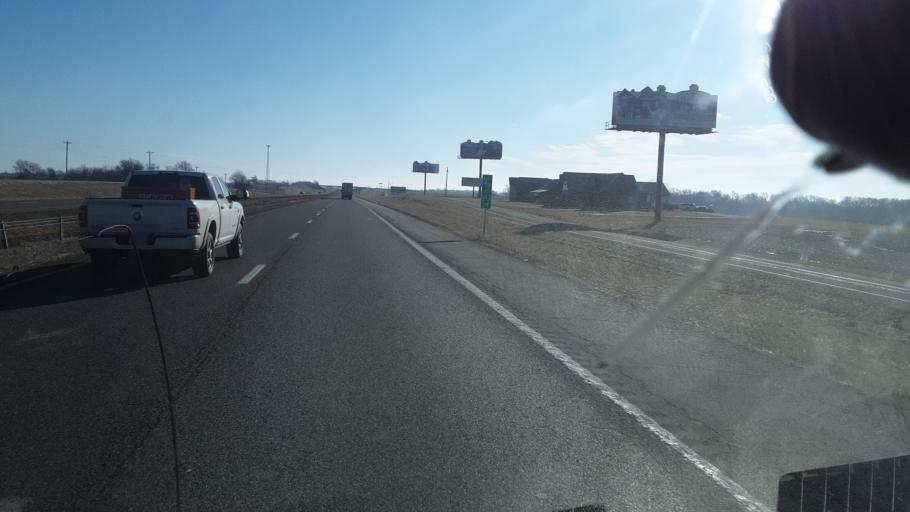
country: US
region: Missouri
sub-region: Callaway County
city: Fulton
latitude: 38.9519
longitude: -92.0224
